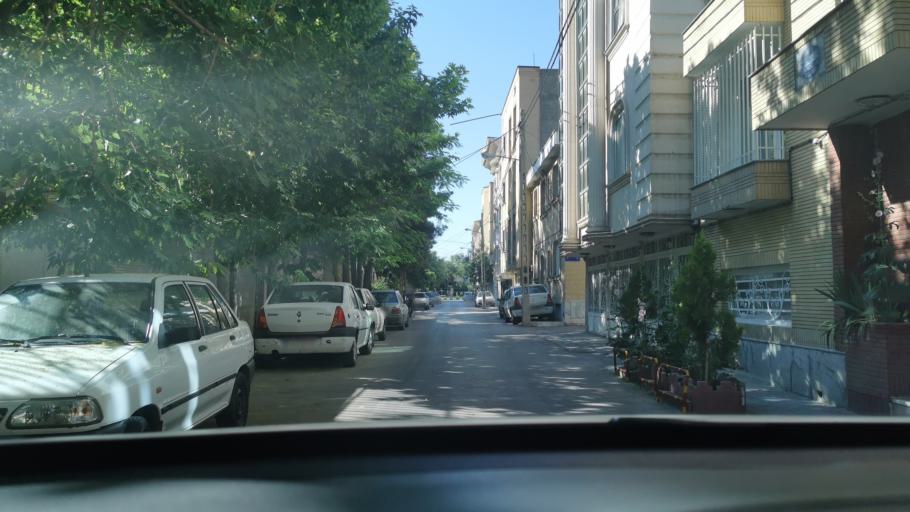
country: IR
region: Razavi Khorasan
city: Mashhad
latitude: 36.2860
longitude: 59.5778
